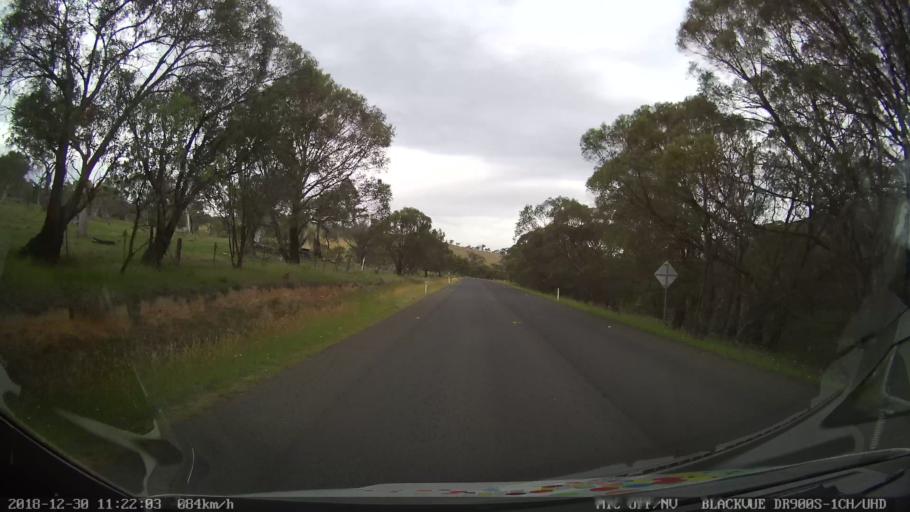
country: AU
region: New South Wales
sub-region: Snowy River
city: Jindabyne
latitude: -36.5046
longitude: 148.6714
